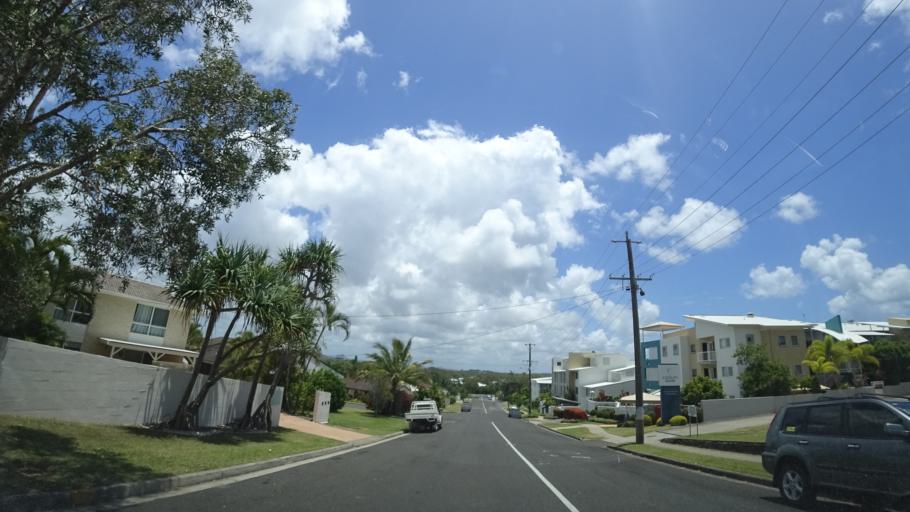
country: AU
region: Queensland
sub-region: Sunshine Coast
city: Coolum Beach
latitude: -26.5329
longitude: 153.0903
